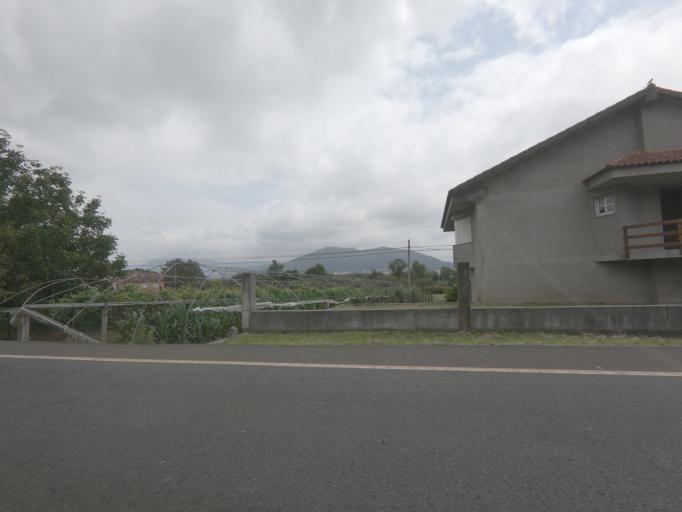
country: ES
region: Galicia
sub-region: Provincia de Pontevedra
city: O Rosal
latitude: 41.9194
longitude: -8.8133
